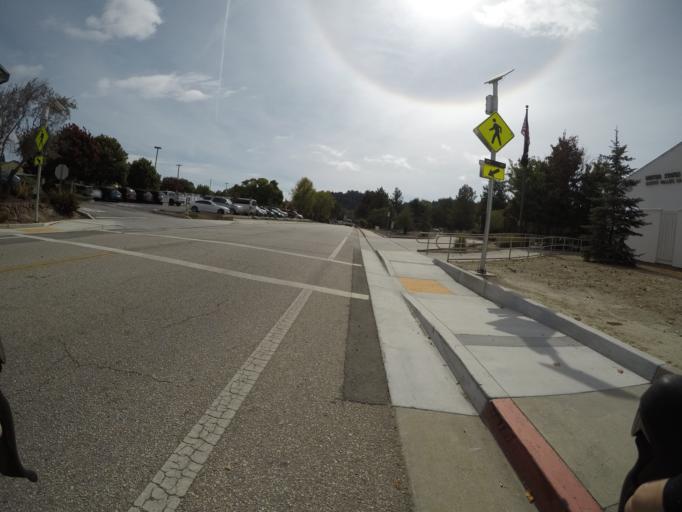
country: US
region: California
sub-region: Santa Cruz County
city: Scotts Valley
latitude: 37.0479
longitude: -122.0282
